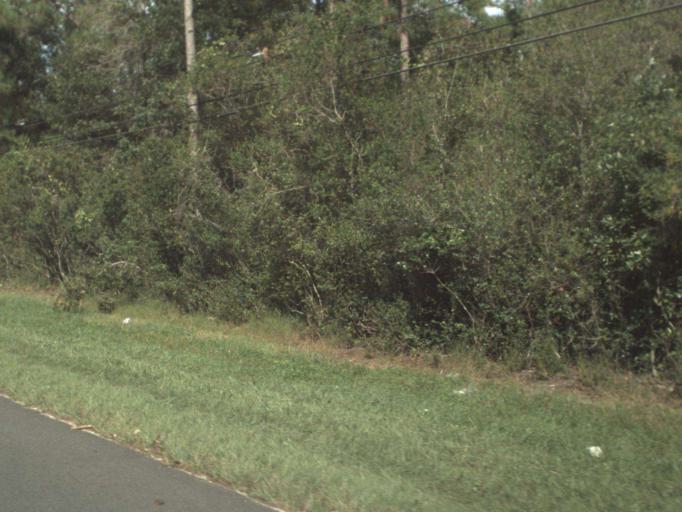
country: US
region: Florida
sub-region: Bay County
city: Cedar Grove
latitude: 30.1841
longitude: -85.6078
